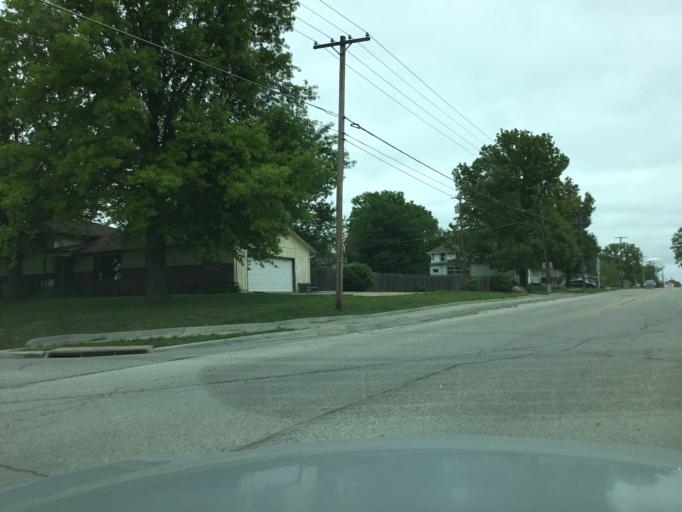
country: US
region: Kansas
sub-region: Franklin County
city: Ottawa
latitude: 38.5938
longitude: -95.2770
